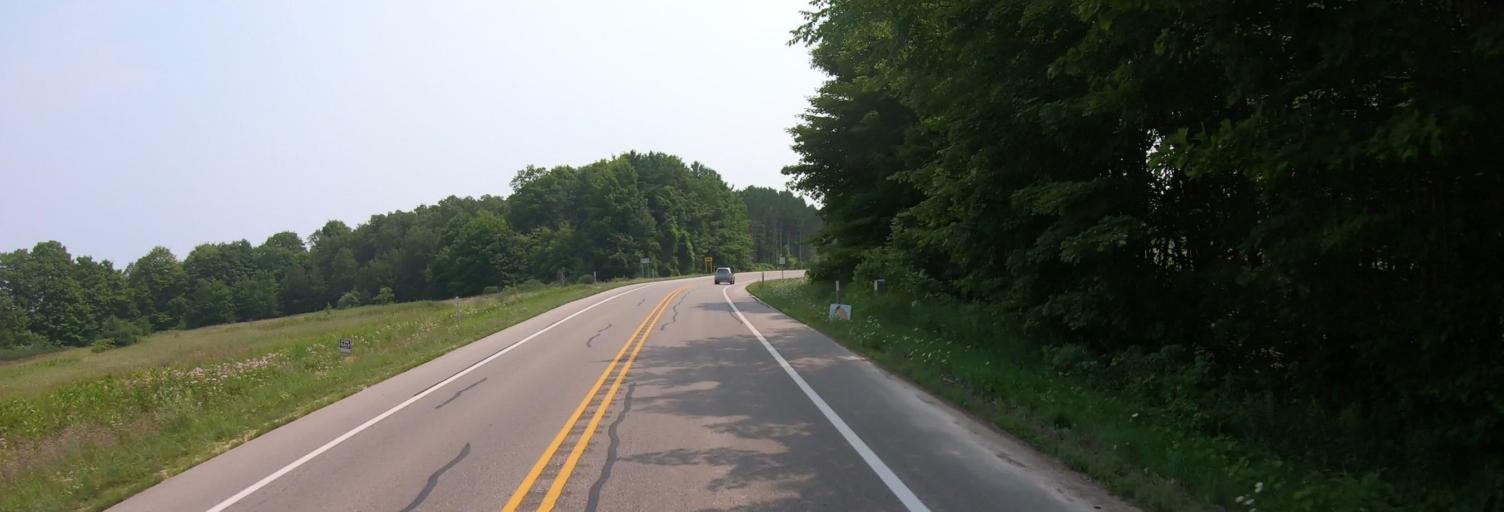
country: US
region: Michigan
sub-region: Leelanau County
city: Leland
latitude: 45.0848
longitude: -85.5966
